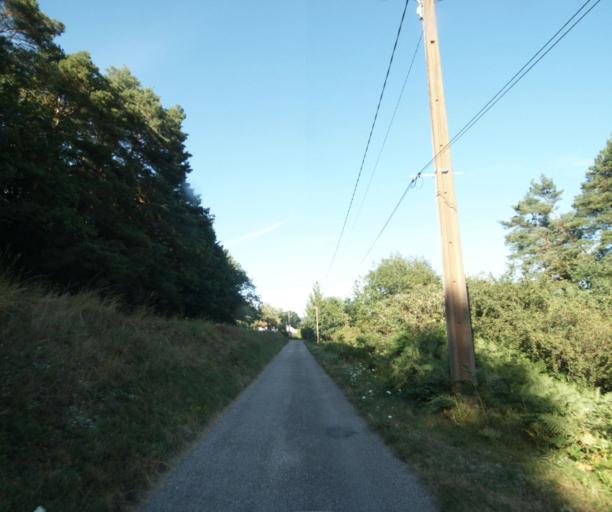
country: FR
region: Lorraine
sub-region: Departement des Vosges
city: Chantraine
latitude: 48.1497
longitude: 6.4428
